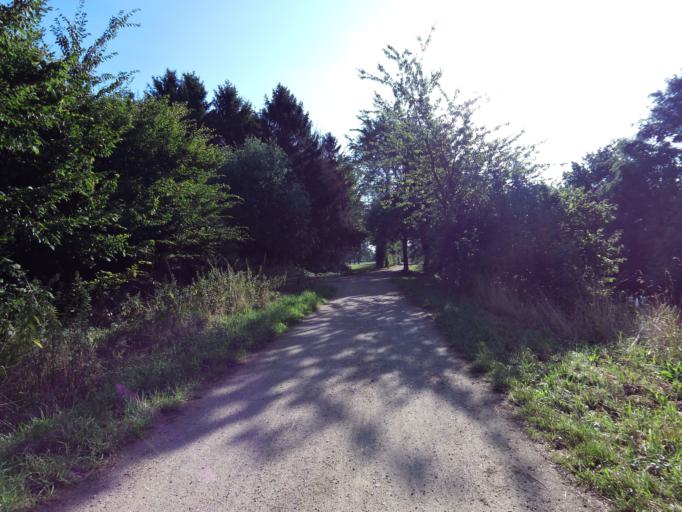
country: DE
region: North Rhine-Westphalia
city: Huckelhoven
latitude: 51.0506
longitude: 6.1992
